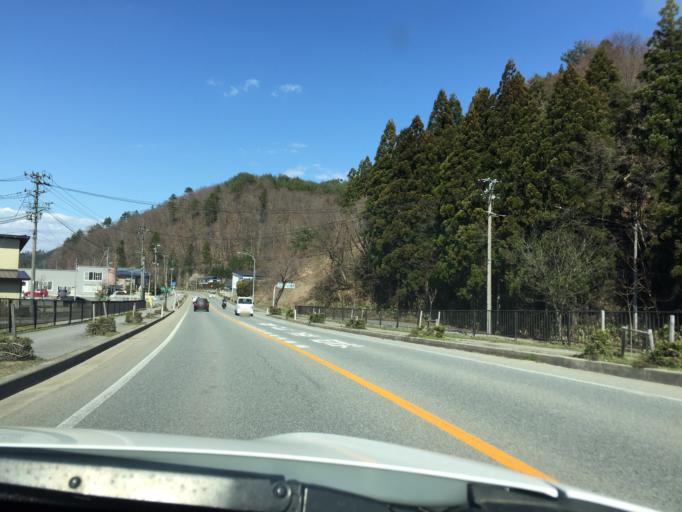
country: JP
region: Yamagata
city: Nagai
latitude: 38.1151
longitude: 140.0489
